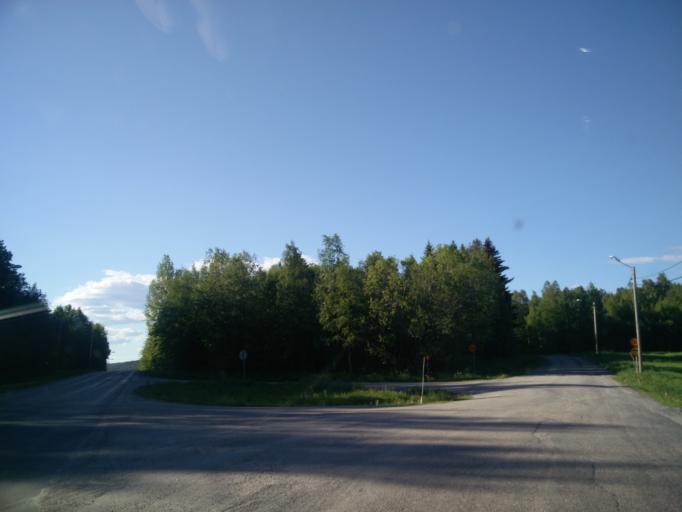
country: SE
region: Vaesternorrland
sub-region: Timra Kommun
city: Timra
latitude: 62.4542
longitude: 17.2641
